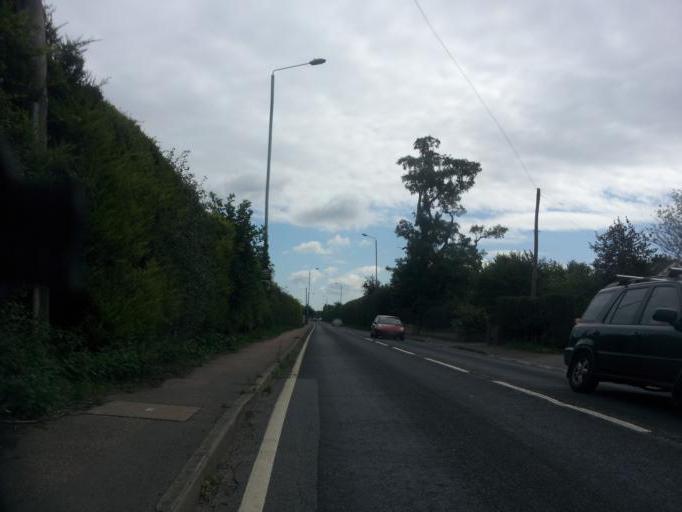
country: GB
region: England
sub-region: Kent
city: Newington
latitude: 51.3540
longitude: 0.6567
